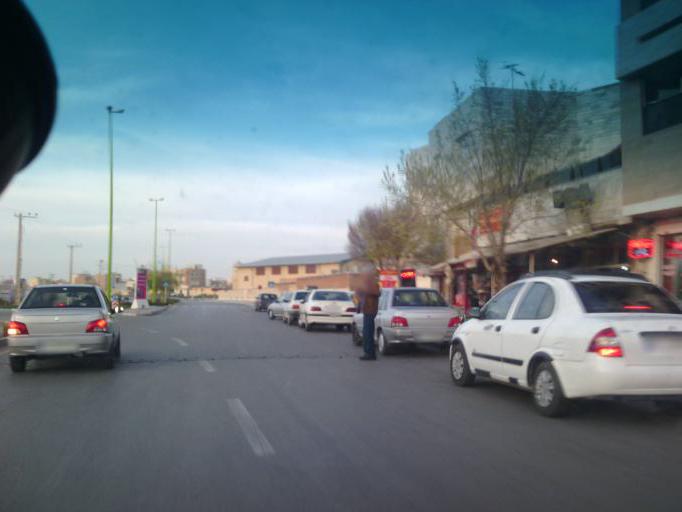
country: IR
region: Isfahan
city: Shahin Shahr
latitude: 32.8683
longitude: 51.5411
